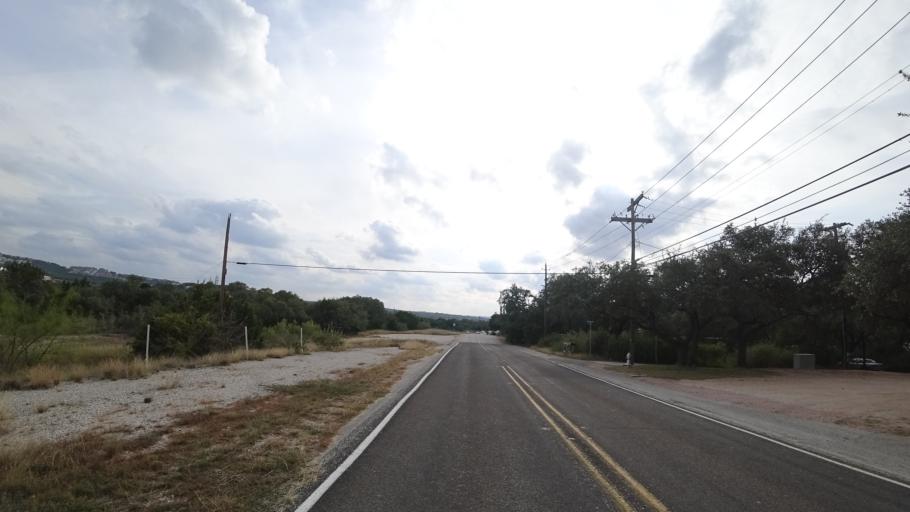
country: US
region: Texas
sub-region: Travis County
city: Hudson Bend
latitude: 30.3922
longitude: -97.8883
